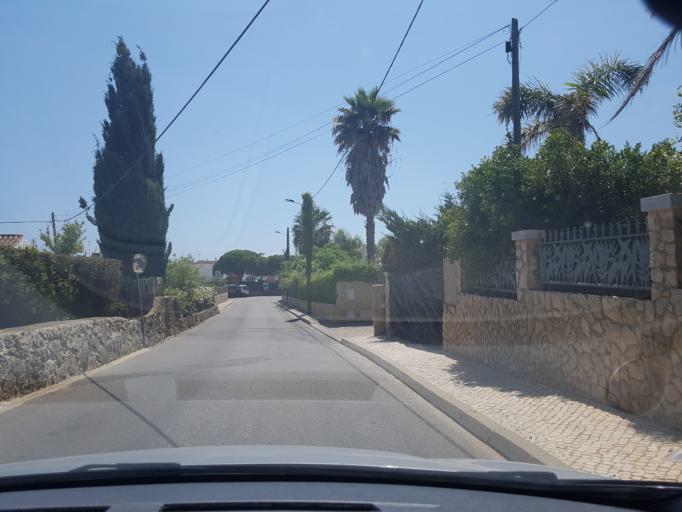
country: PT
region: Faro
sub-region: Lagoa
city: Carvoeiro
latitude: 37.0958
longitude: -8.4624
